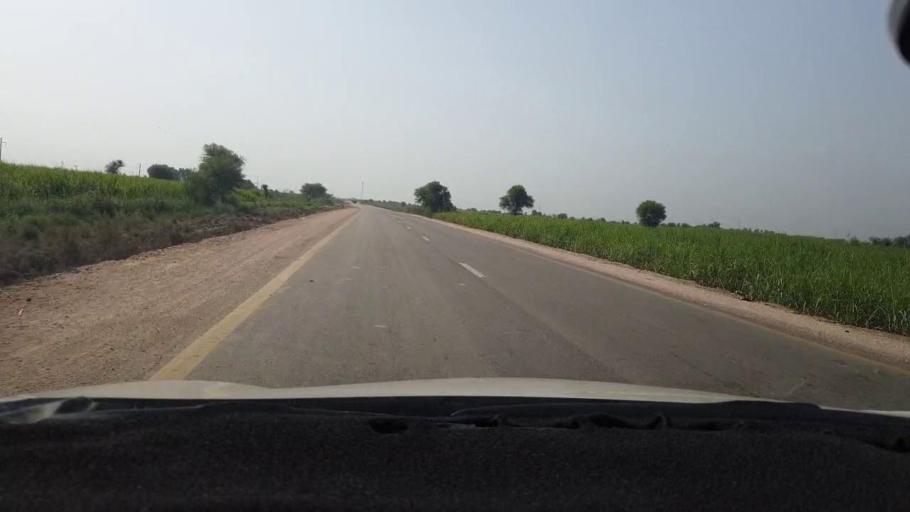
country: PK
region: Sindh
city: Jhol
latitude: 25.8440
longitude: 69.0616
